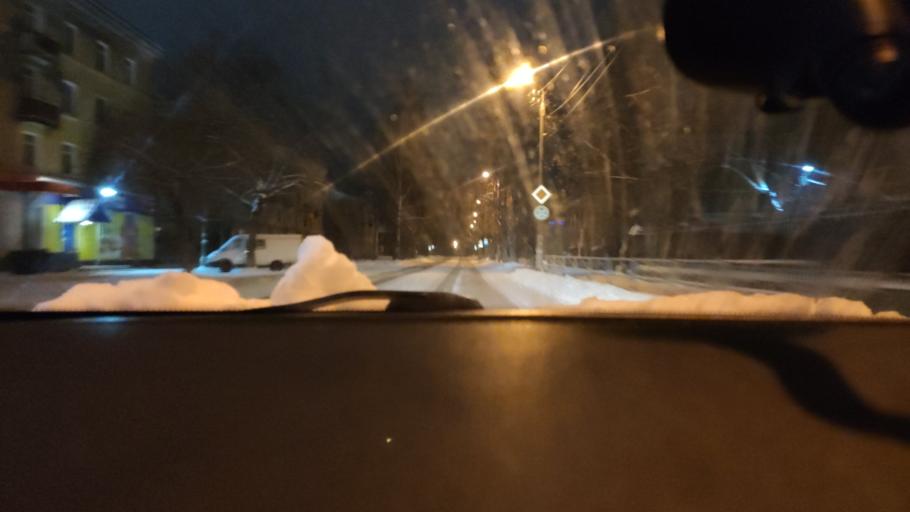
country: RU
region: Perm
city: Krasnokamsk
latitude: 58.0861
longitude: 55.7644
